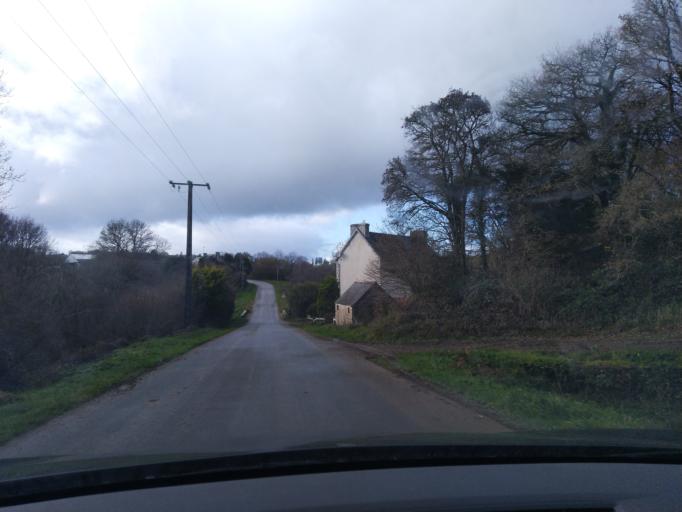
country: FR
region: Brittany
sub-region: Departement du Finistere
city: Guerlesquin
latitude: 48.4257
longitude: -3.6173
